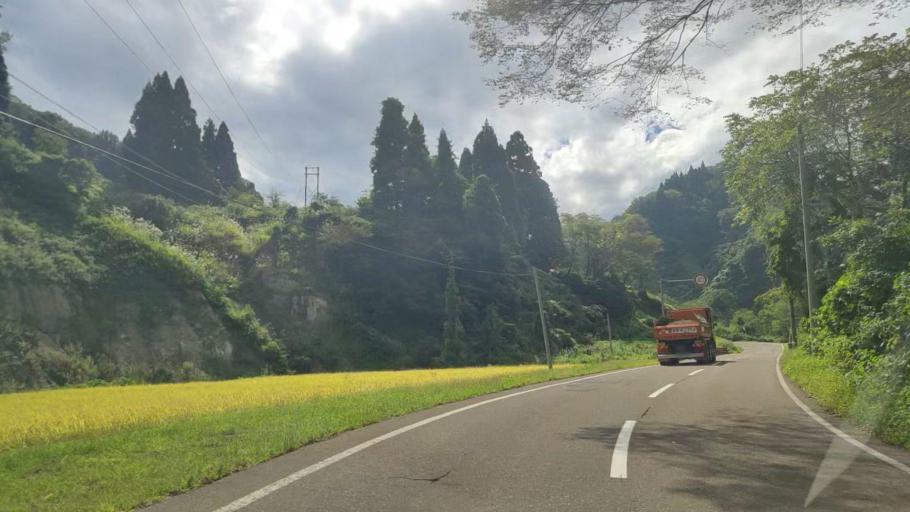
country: JP
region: Niigata
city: Arai
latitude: 36.9421
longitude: 138.2916
